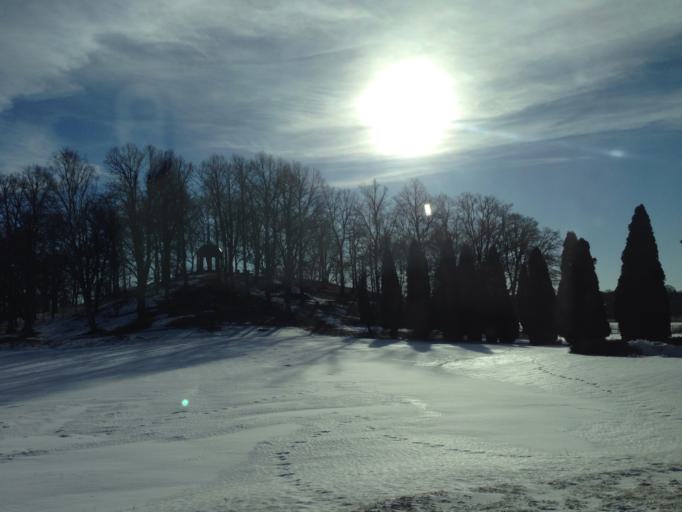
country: SE
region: Stockholm
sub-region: Ekero Kommun
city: Ekeroe
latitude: 59.2939
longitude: 17.8291
